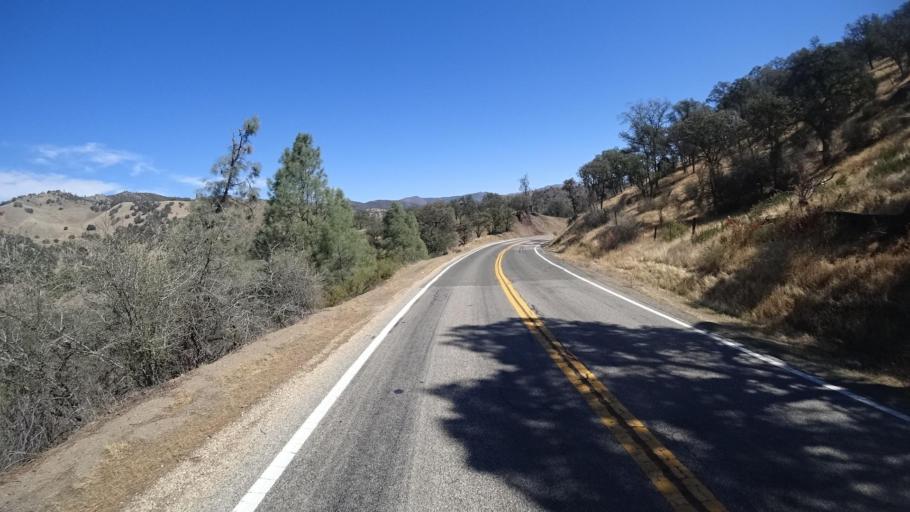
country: US
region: California
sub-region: Monterey County
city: King City
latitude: 36.1957
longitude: -120.7467
